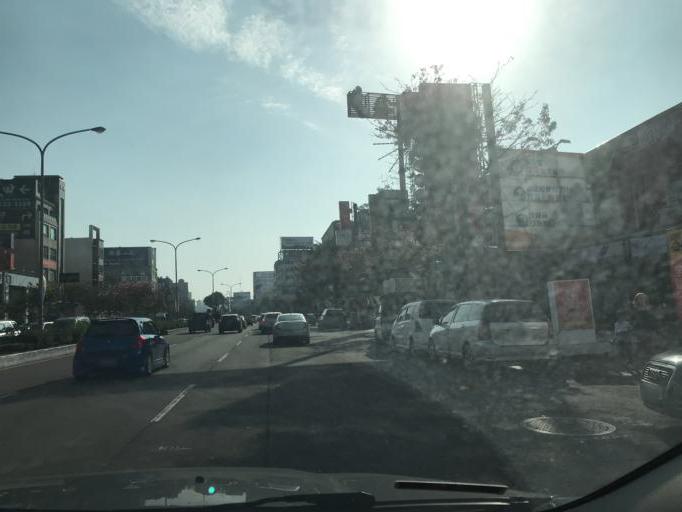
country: TW
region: Taiwan
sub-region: Hsinchu
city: Zhubei
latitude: 24.8166
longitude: 121.0254
